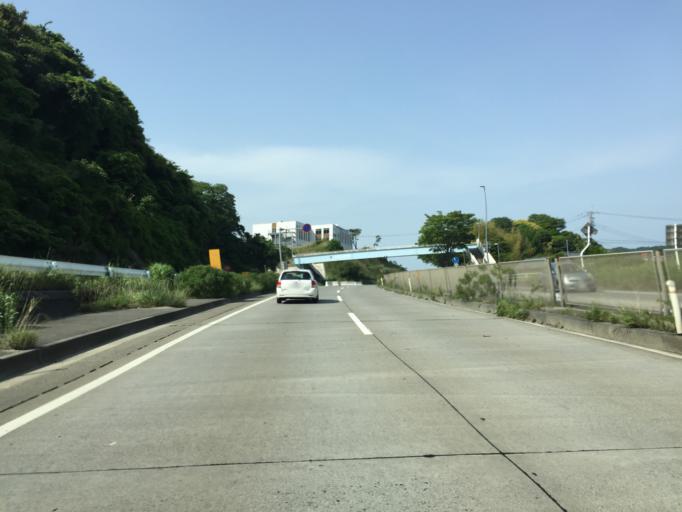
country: JP
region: Fukushima
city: Iwaki
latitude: 36.9611
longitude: 140.8798
